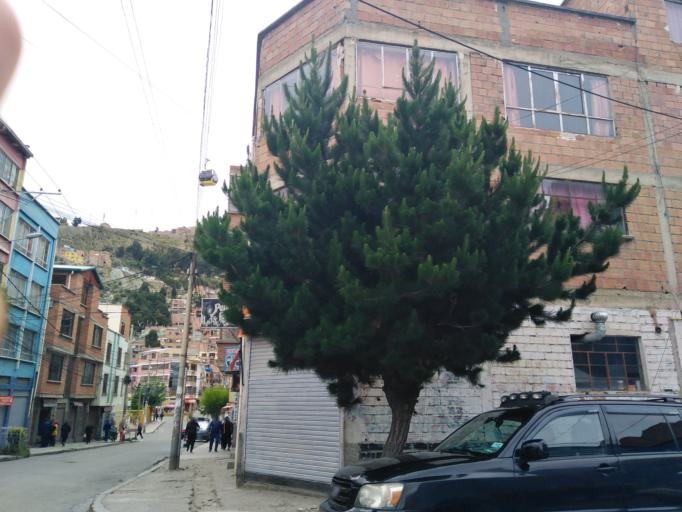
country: BO
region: La Paz
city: La Paz
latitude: -16.5149
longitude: -68.1391
